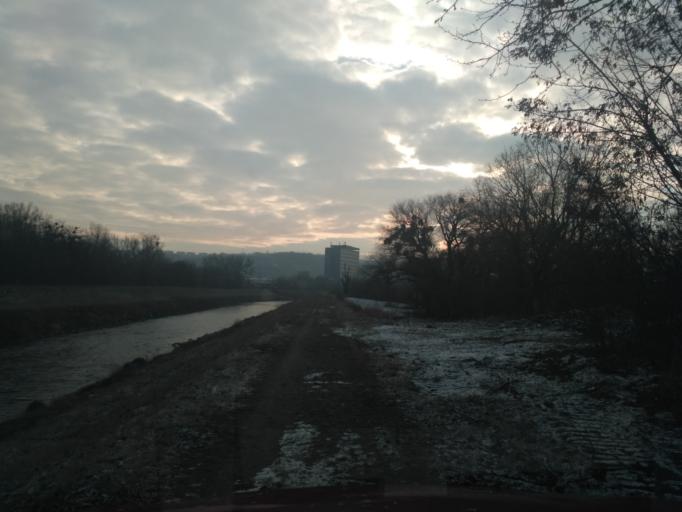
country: SK
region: Kosicky
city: Kosice
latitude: 48.7323
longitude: 21.2681
